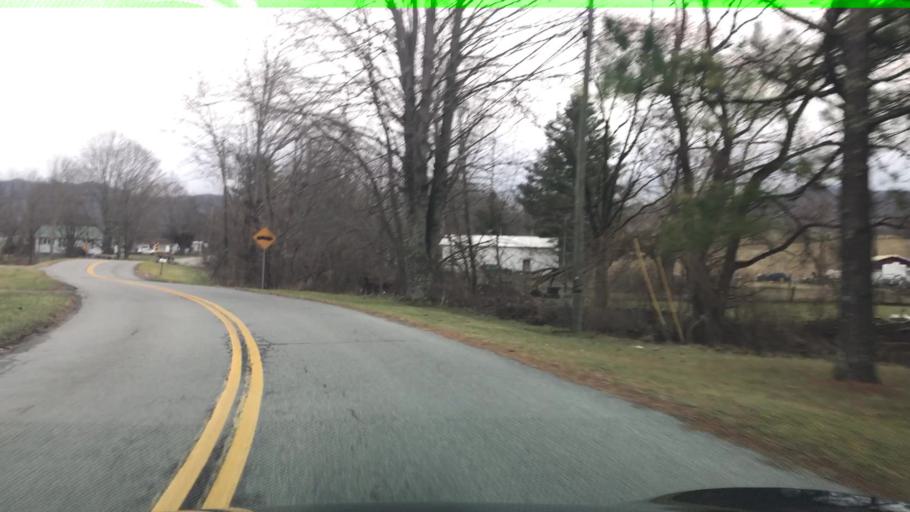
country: US
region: Virginia
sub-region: Smyth County
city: Atkins
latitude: 36.7747
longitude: -81.4118
